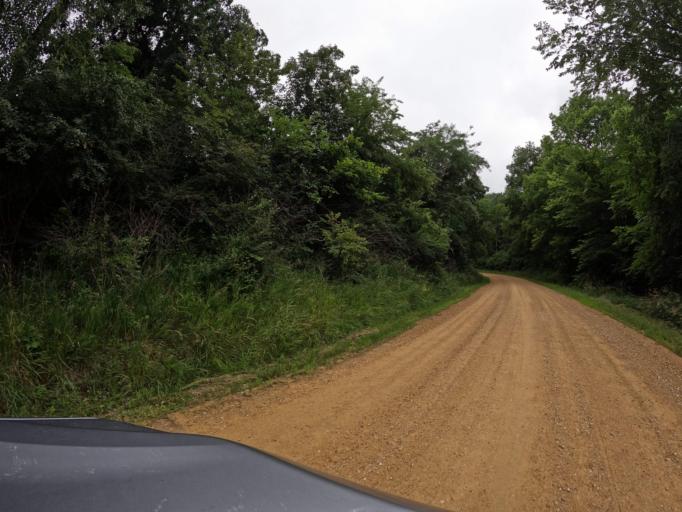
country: US
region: Illinois
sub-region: Carroll County
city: Savanna
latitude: 41.9829
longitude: -90.1749
